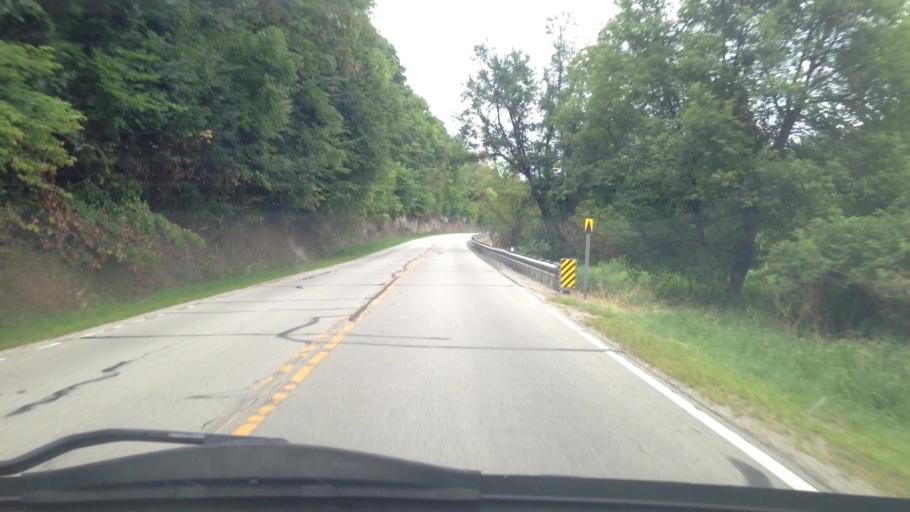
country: US
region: Minnesota
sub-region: Fillmore County
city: Preston
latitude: 43.7323
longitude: -91.9651
